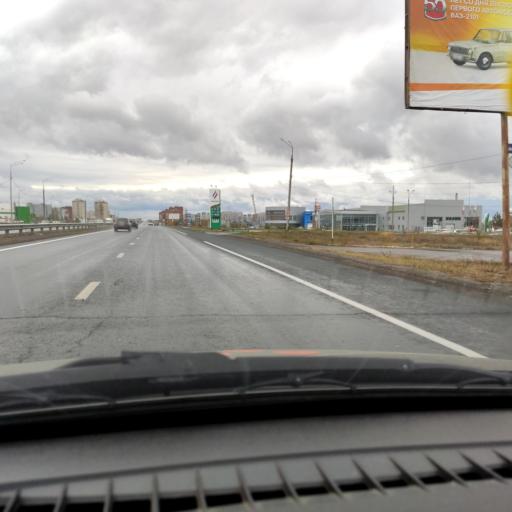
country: RU
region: Samara
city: Tol'yatti
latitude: 53.5543
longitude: 49.3430
